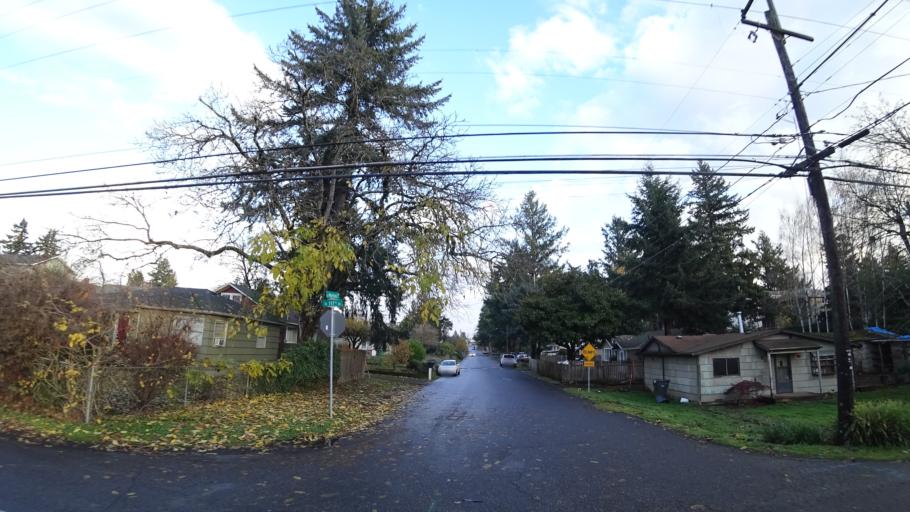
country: US
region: Oregon
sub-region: Multnomah County
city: Lents
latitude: 45.5169
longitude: -122.5429
